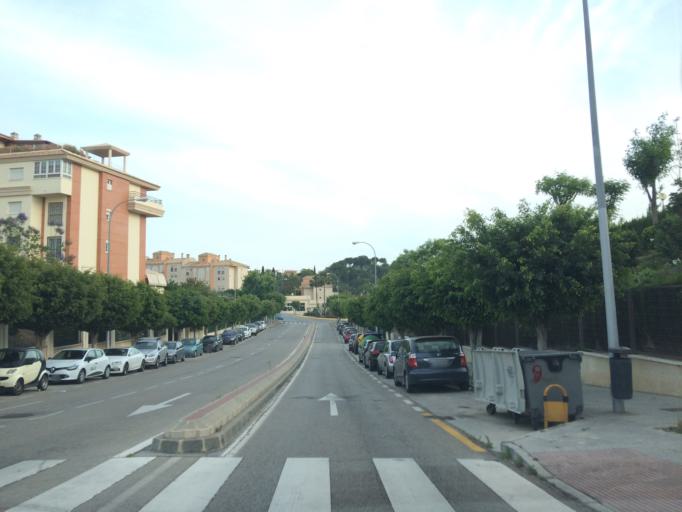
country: ES
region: Andalusia
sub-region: Provincia de Malaga
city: Malaga
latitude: 36.7292
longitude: -4.3894
